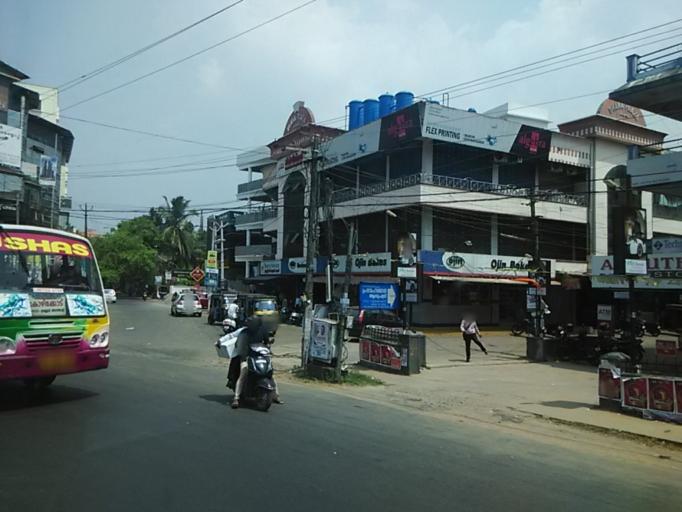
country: IN
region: Kerala
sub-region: Kozhikode
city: Kozhikode
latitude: 11.2729
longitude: 75.7751
